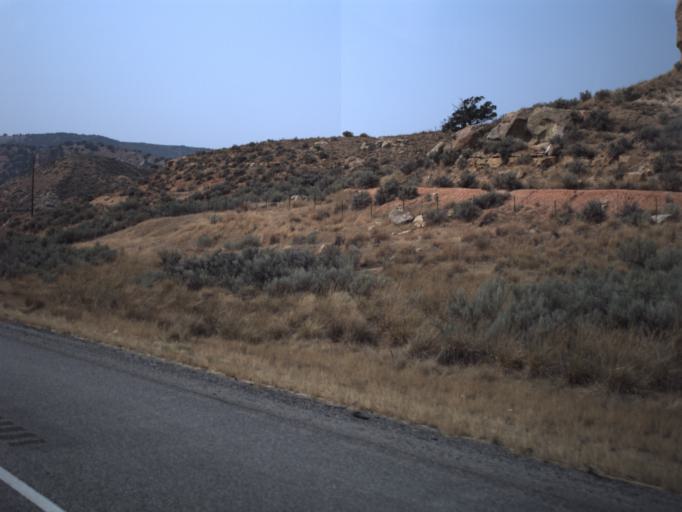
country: US
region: Wyoming
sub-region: Uinta County
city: Evanston
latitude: 41.1237
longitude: -111.1781
